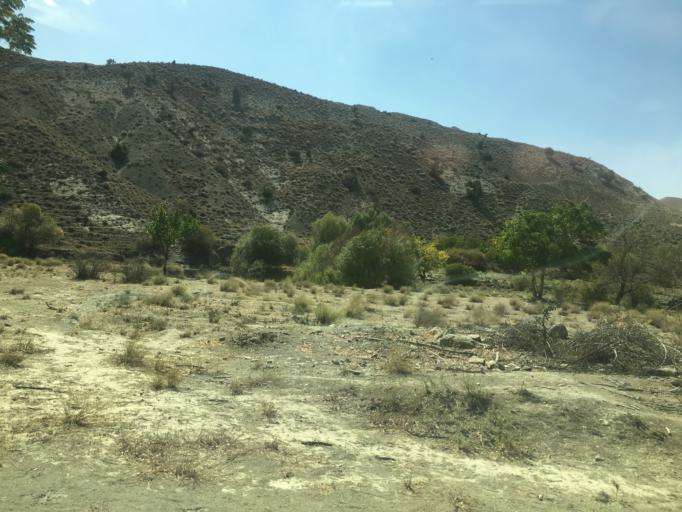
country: TM
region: Ahal
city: Baharly
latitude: 38.3560
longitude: 57.0905
